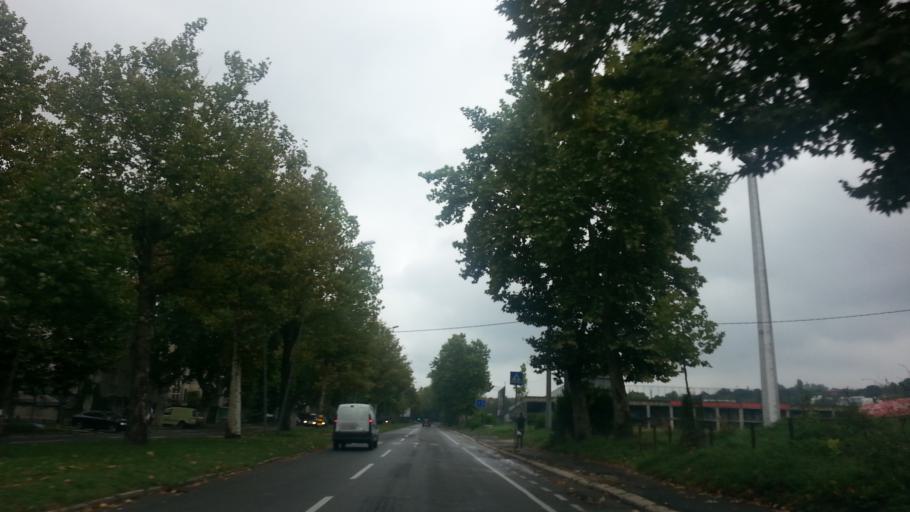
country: RS
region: Central Serbia
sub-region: Belgrade
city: Vozdovac
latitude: 44.7836
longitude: 20.4664
